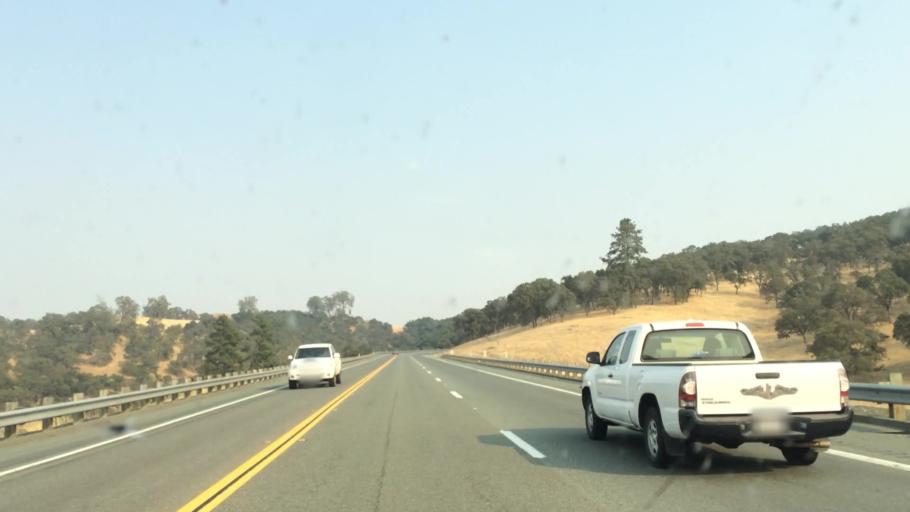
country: US
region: California
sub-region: Amador County
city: Sutter Creek
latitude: 38.4152
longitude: -120.8391
